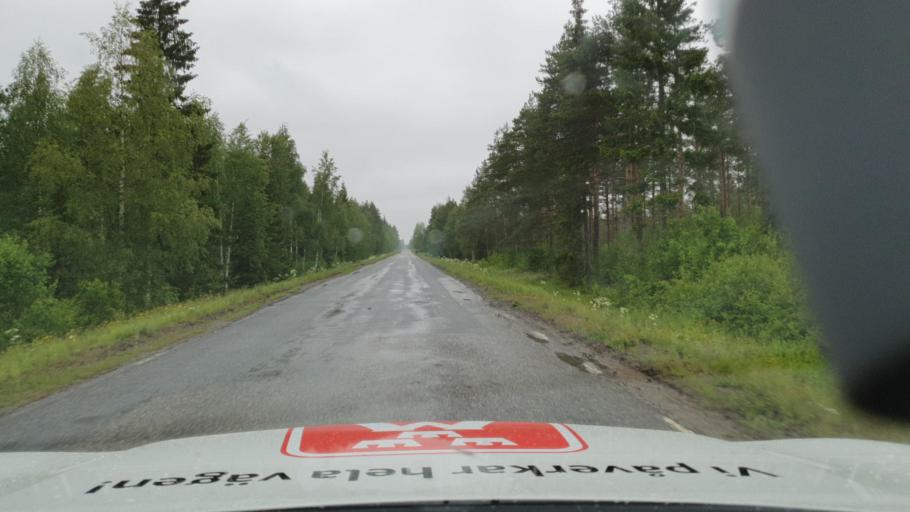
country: SE
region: Vaesterbotten
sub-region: Nordmalings Kommun
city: Nordmaling
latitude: 63.8147
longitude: 19.4978
